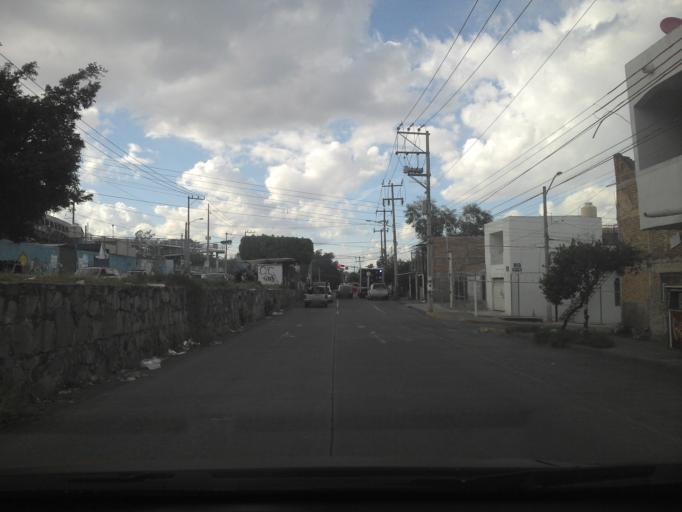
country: MX
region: Jalisco
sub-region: Tlajomulco de Zuniga
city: Altus Bosques
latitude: 20.6175
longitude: -103.3729
